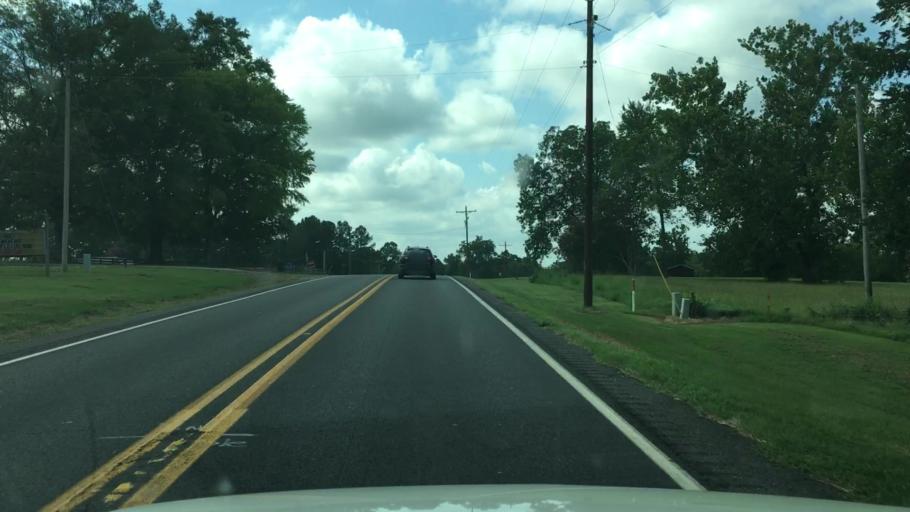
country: US
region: Arkansas
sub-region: Garland County
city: Lake Hamilton
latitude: 34.3263
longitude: -93.1735
